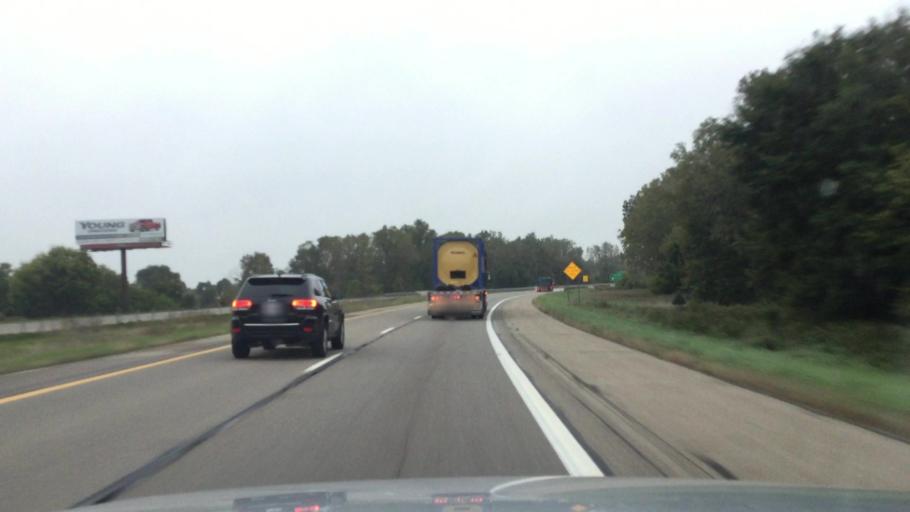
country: US
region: Michigan
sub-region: Shiawassee County
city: Durand
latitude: 42.9307
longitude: -83.9927
